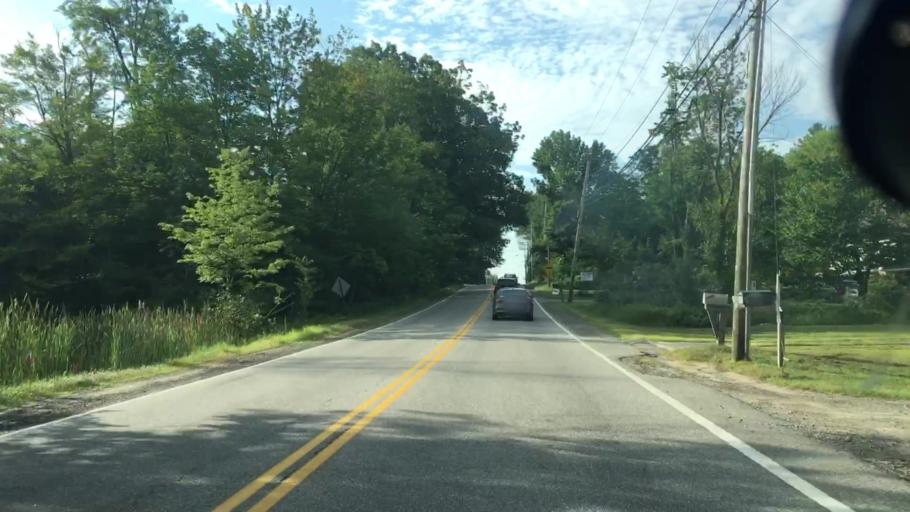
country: US
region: Maine
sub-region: Cumberland County
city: Westbrook
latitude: 43.7286
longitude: -70.3432
